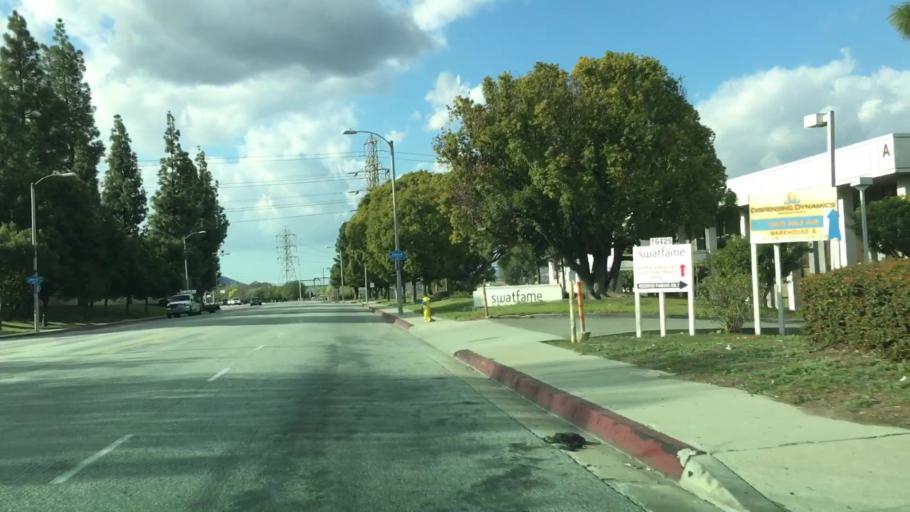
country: US
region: California
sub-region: Los Angeles County
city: La Puente
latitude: 34.0055
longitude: -117.9461
